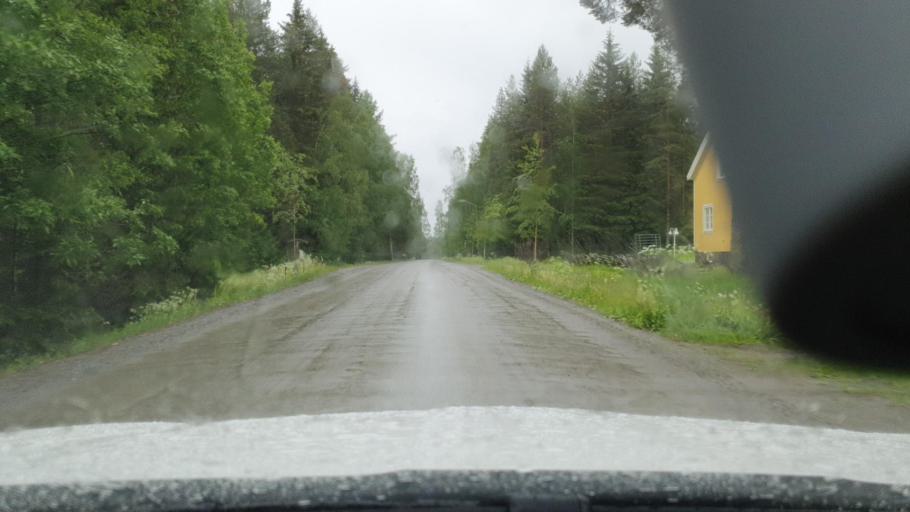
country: SE
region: Vaesterbotten
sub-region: Skelleftea Kommun
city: Burtraesk
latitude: 64.3491
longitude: 20.4873
